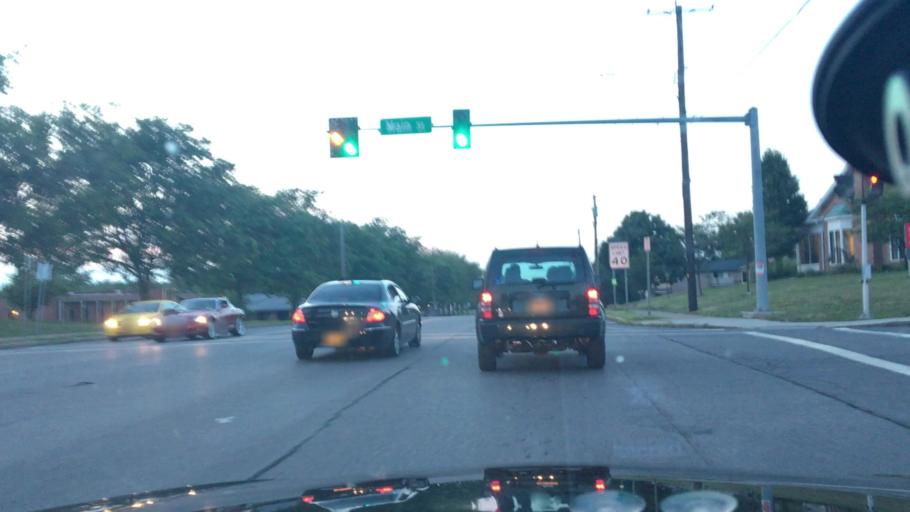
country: US
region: New York
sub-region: Erie County
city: West Seneca
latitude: 42.8334
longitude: -78.7537
